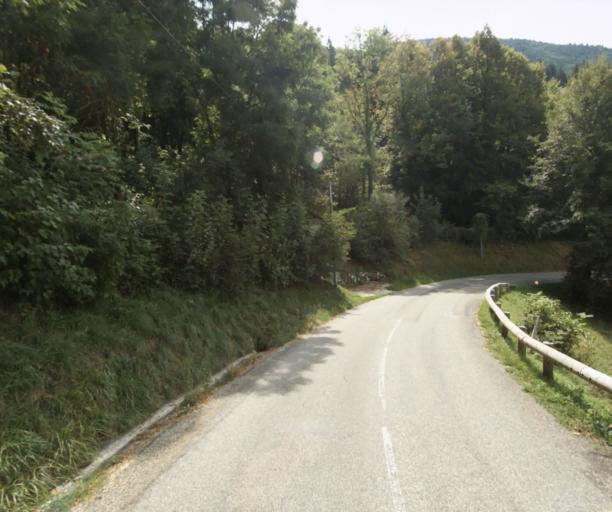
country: FR
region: Rhone-Alpes
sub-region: Departement de l'Isere
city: Le Sappey-en-Chartreuse
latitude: 45.2624
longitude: 5.7494
